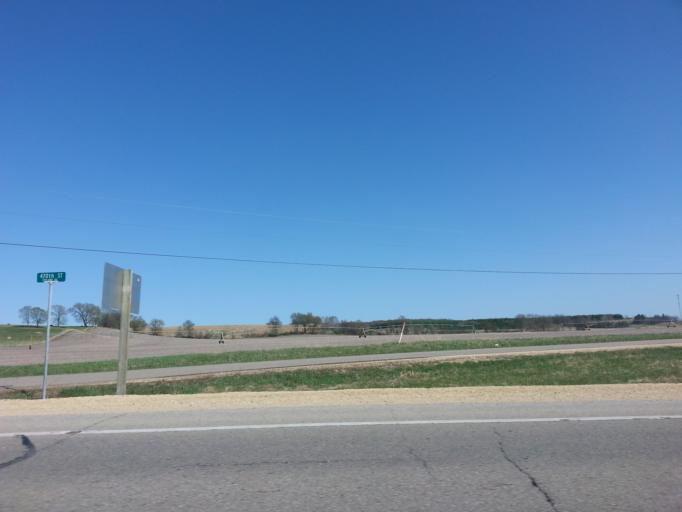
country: US
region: Wisconsin
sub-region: Dunn County
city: Menomonie
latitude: 44.7818
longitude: -91.9239
